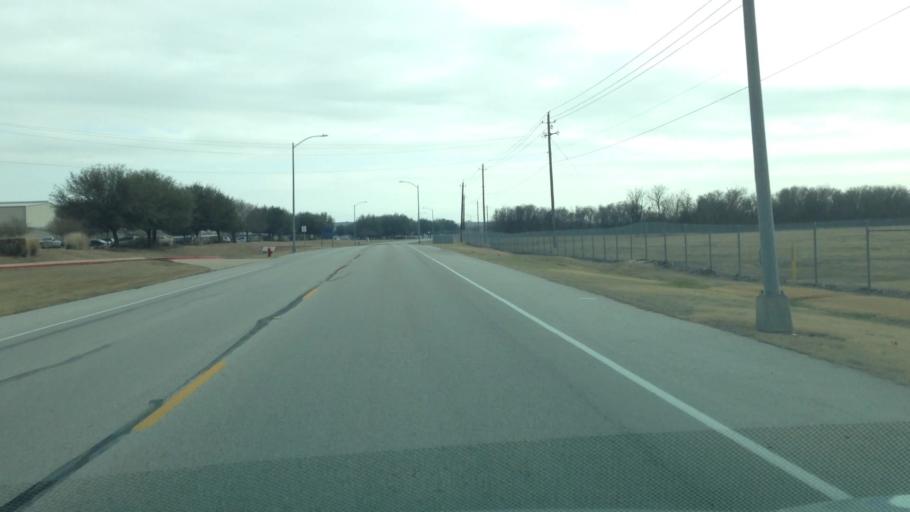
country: US
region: Texas
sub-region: Travis County
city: Hornsby Bend
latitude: 30.1893
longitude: -97.6636
